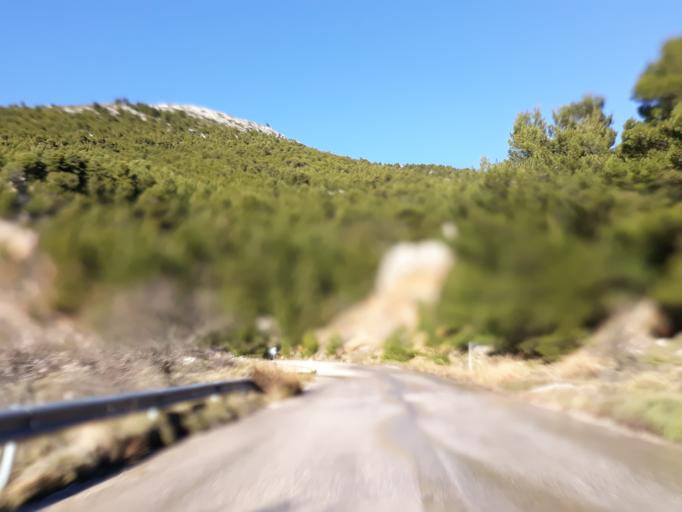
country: GR
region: Attica
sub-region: Nomarchia Dytikis Attikis
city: Fyli
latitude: 38.1444
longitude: 23.6450
